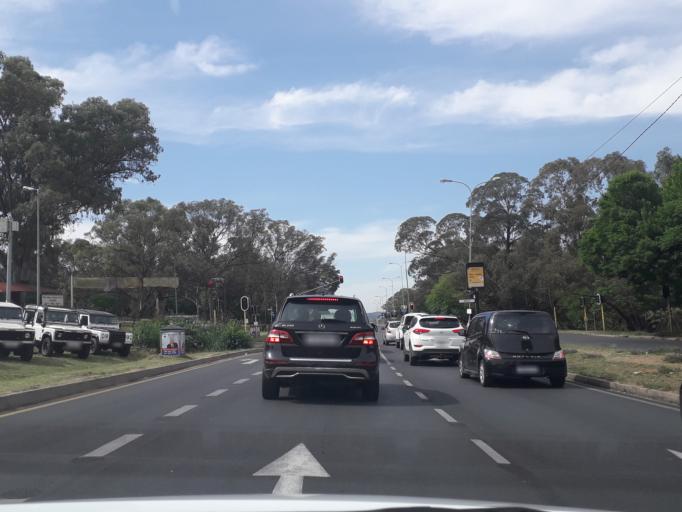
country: ZA
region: Gauteng
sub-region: City of Johannesburg Metropolitan Municipality
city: Diepsloot
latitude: -26.0322
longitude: 28.0270
